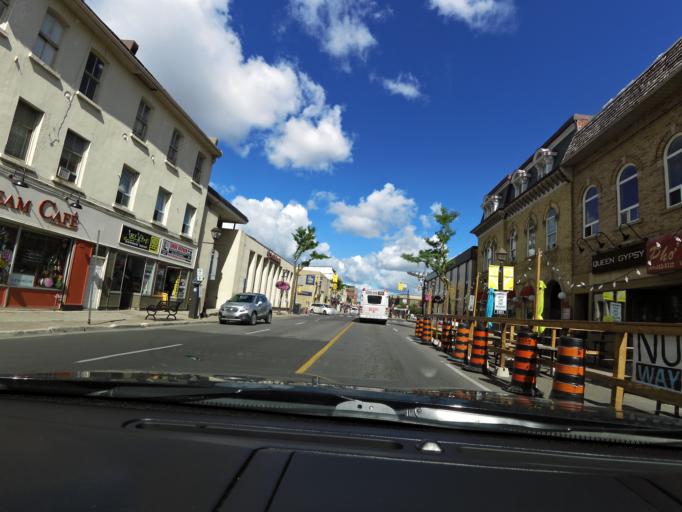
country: CA
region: Ontario
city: Brampton
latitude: 43.6855
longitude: -79.7594
